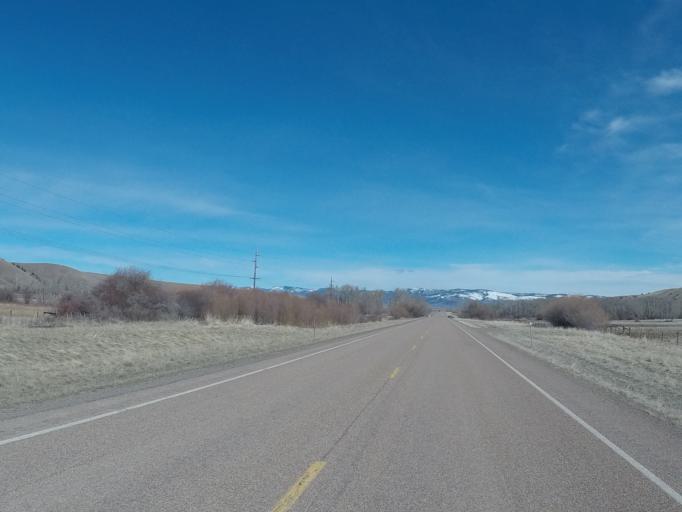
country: US
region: Montana
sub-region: Granite County
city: Philipsburg
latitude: 46.5263
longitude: -113.2246
